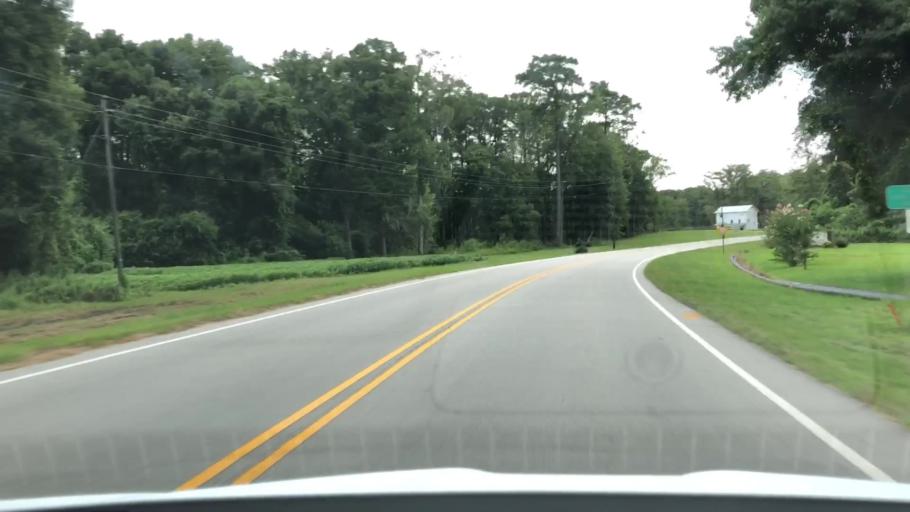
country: US
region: North Carolina
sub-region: Jones County
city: Trenton
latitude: 35.0574
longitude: -77.3571
